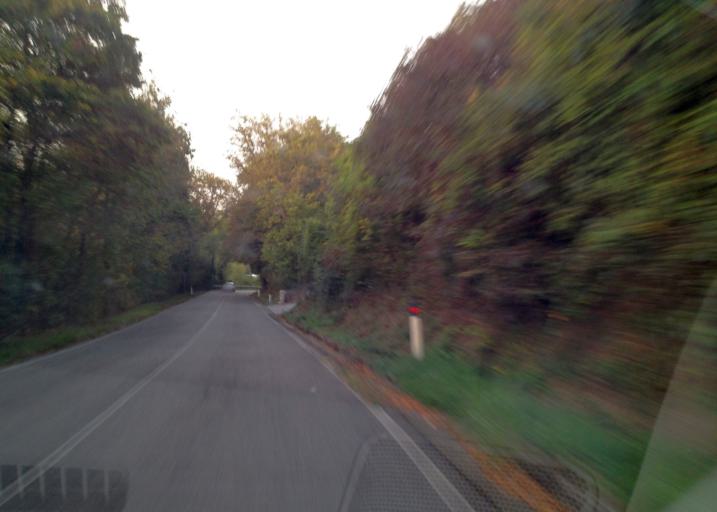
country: IT
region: Tuscany
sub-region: Province of Florence
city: Panzano in Chianti
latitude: 43.5142
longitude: 11.2912
